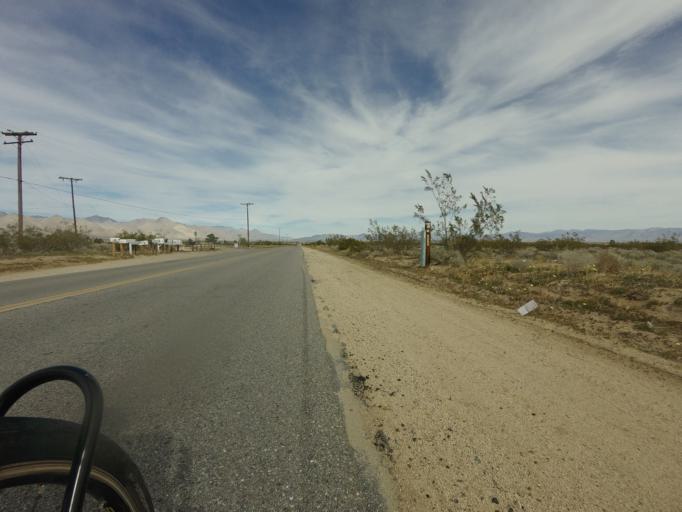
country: US
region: California
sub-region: Kern County
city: Inyokern
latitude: 35.6918
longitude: -117.8256
